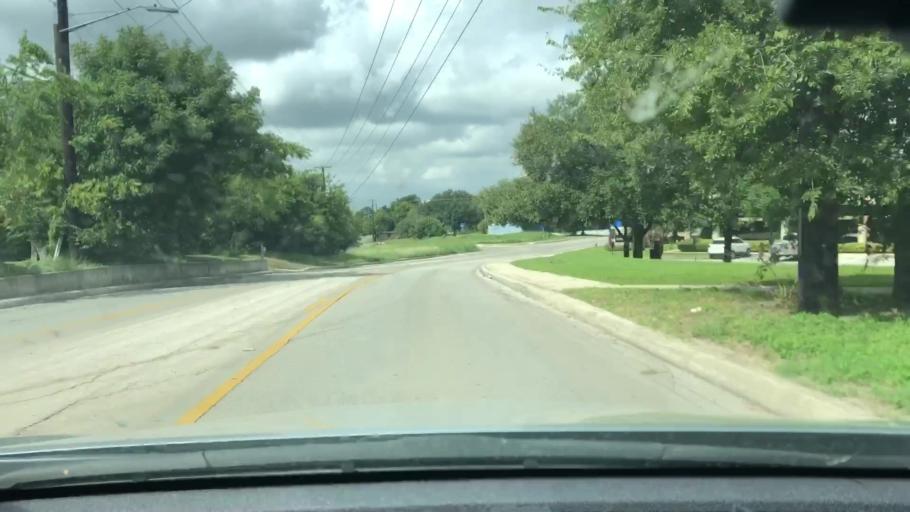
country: US
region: Texas
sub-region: Bexar County
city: Windcrest
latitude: 29.5315
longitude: -98.3766
